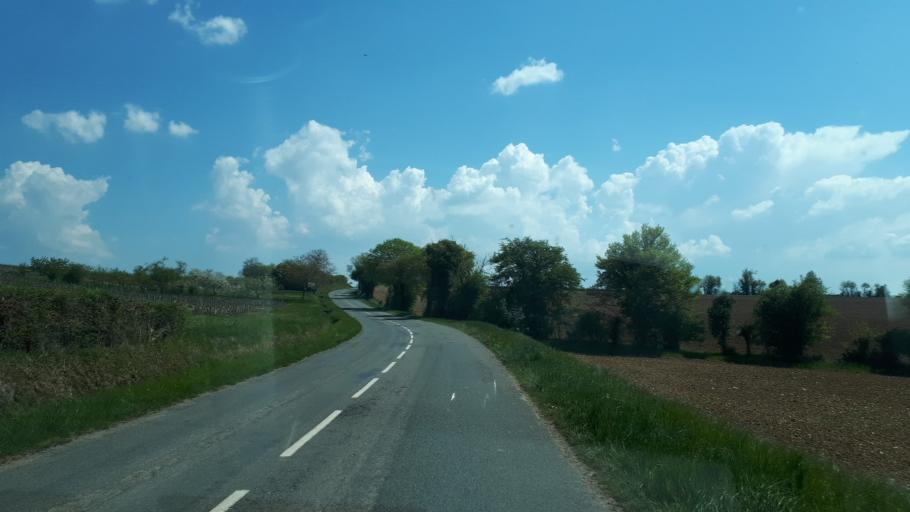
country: FR
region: Centre
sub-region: Departement du Cher
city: Sancerre
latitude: 47.3043
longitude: 2.7342
